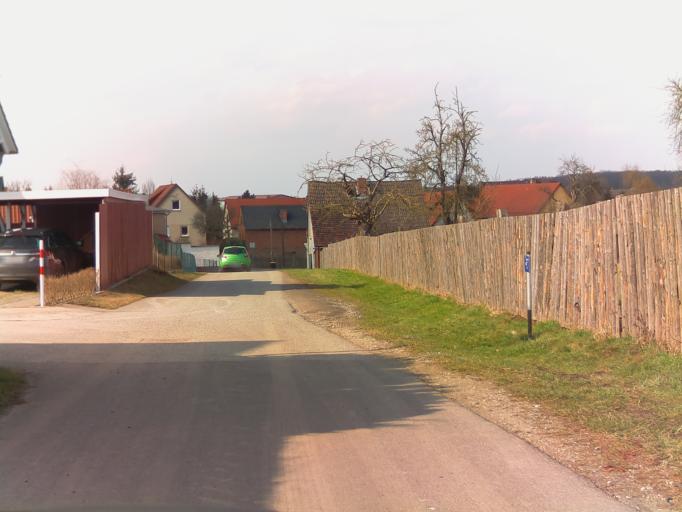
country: DE
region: Saxony-Anhalt
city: Leissling
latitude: 51.1559
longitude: 11.8958
